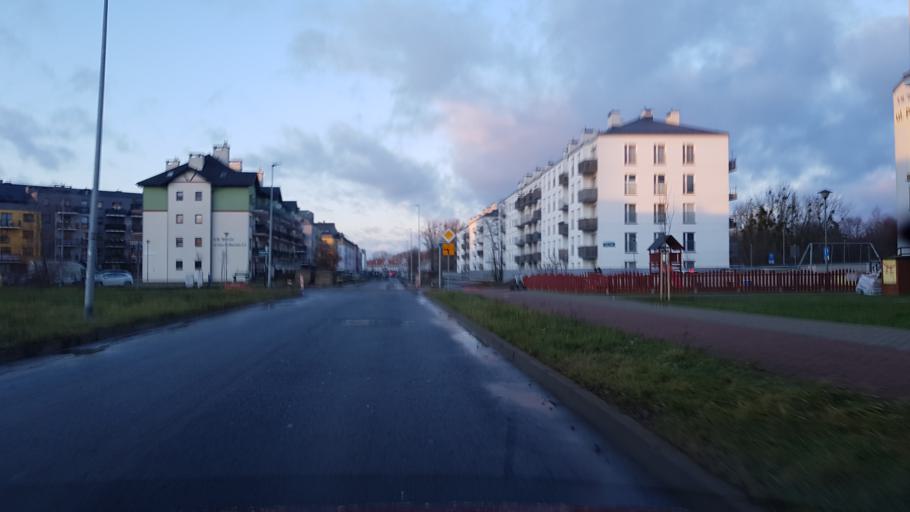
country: PL
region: West Pomeranian Voivodeship
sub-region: Powiat policki
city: Przeclaw
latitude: 53.4283
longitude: 14.4873
